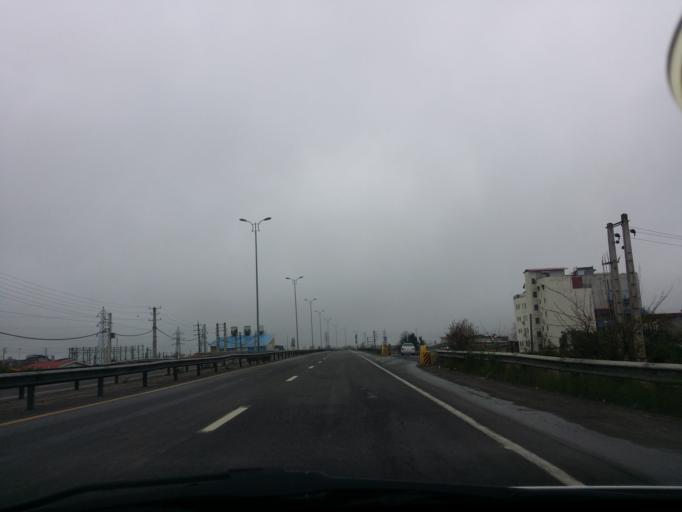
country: IR
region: Mazandaran
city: Tonekabon
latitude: 36.8090
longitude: 50.8634
